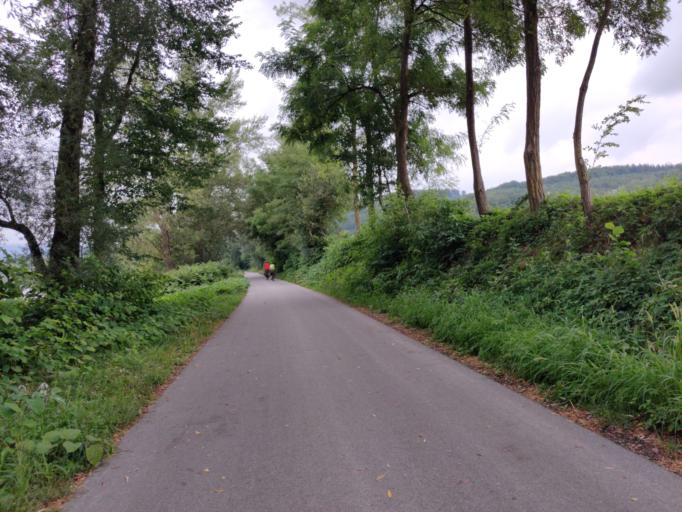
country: AT
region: Lower Austria
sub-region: Politischer Bezirk Melk
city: Ybbs an der Donau
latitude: 48.1763
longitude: 15.1201
